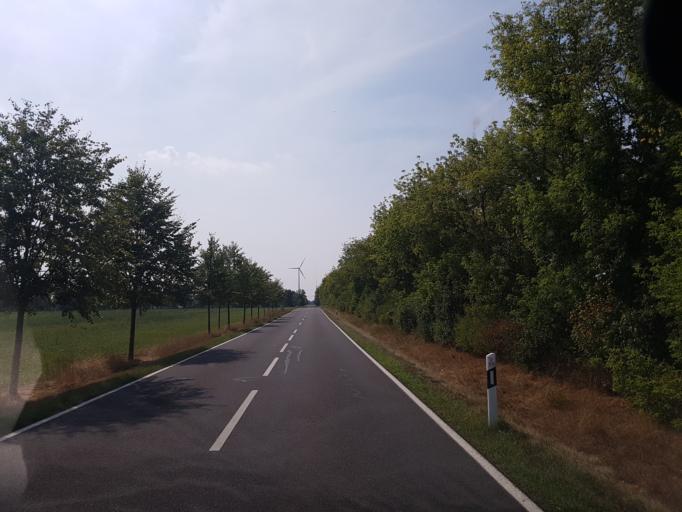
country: DE
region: Brandenburg
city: Finsterwalde
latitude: 51.6611
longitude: 13.7360
